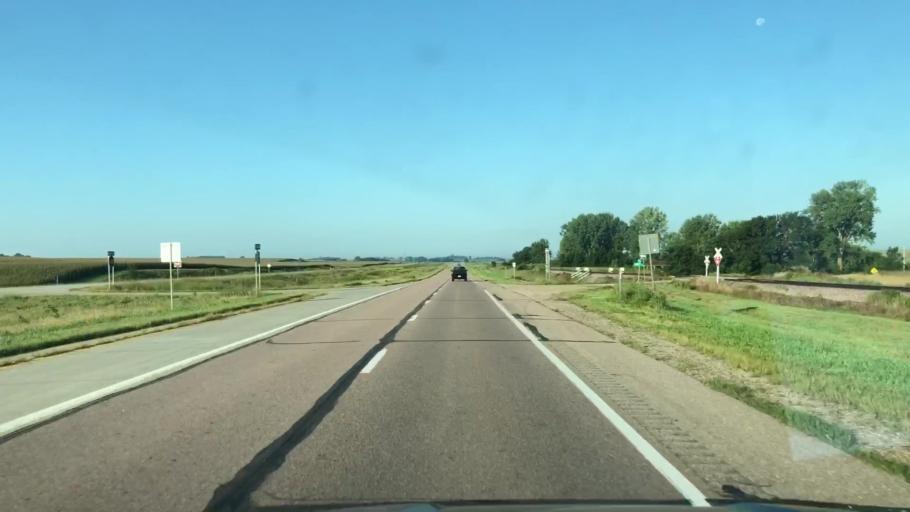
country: US
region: Iowa
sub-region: Sioux County
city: Alton
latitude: 43.0261
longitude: -95.9418
